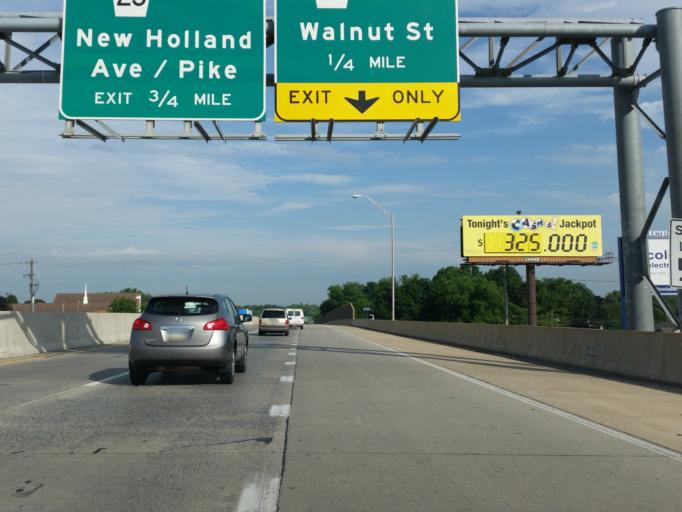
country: US
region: Pennsylvania
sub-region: Lancaster County
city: Lancaster
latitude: 40.0523
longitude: -76.2609
